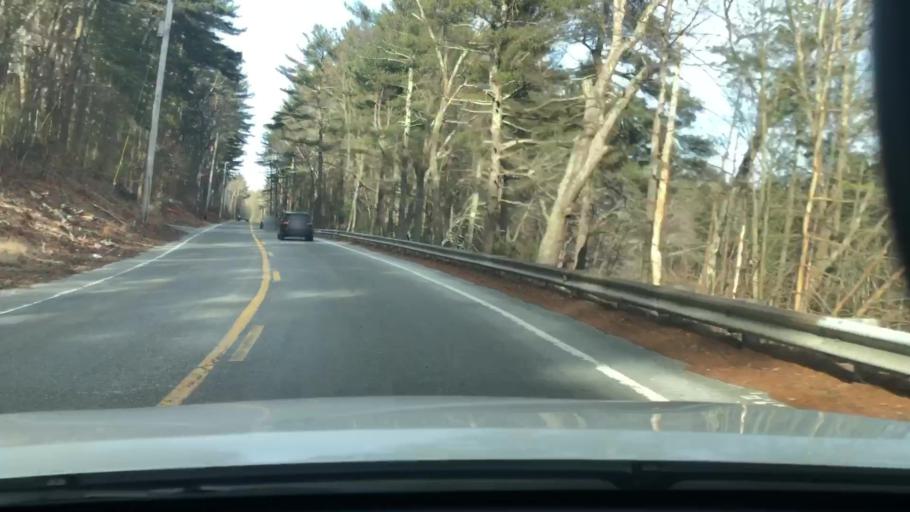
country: US
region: Massachusetts
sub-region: Worcester County
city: Grafton
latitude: 42.1948
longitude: -71.6559
